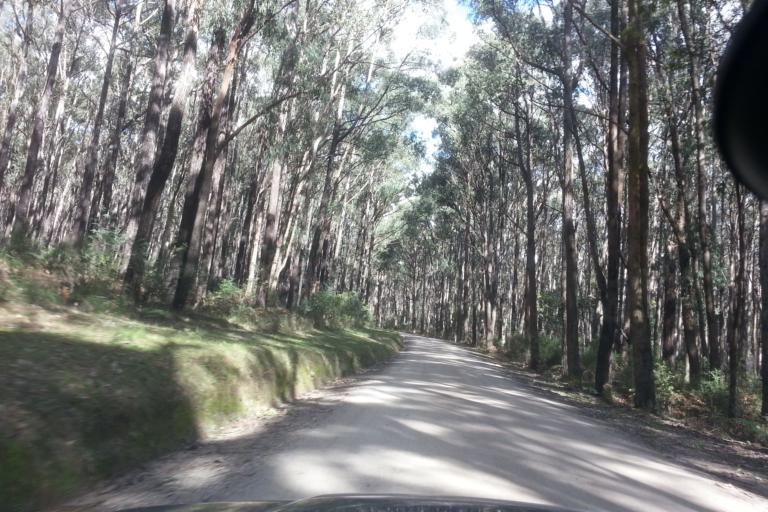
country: AU
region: Victoria
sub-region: Yarra Ranges
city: Mount Dandenong
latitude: -37.8310
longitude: 145.3982
